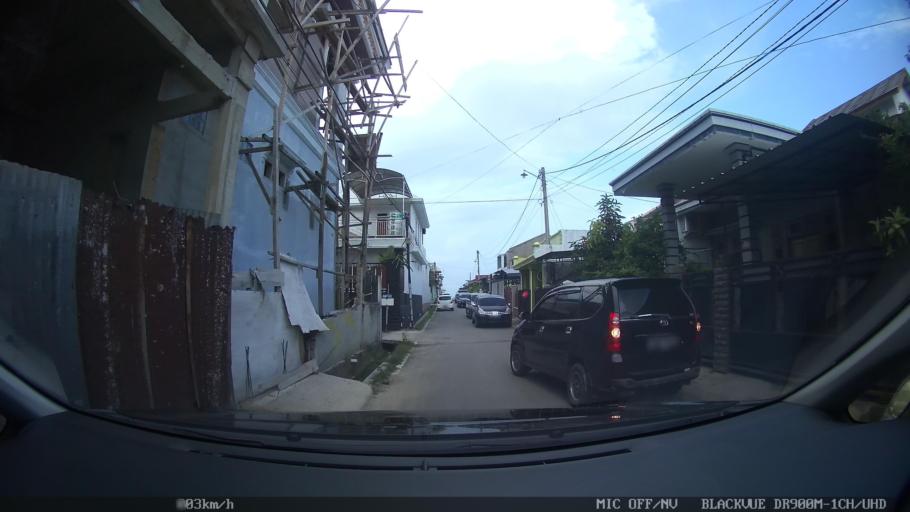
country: ID
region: Lampung
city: Kedaton
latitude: -5.3982
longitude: 105.2093
